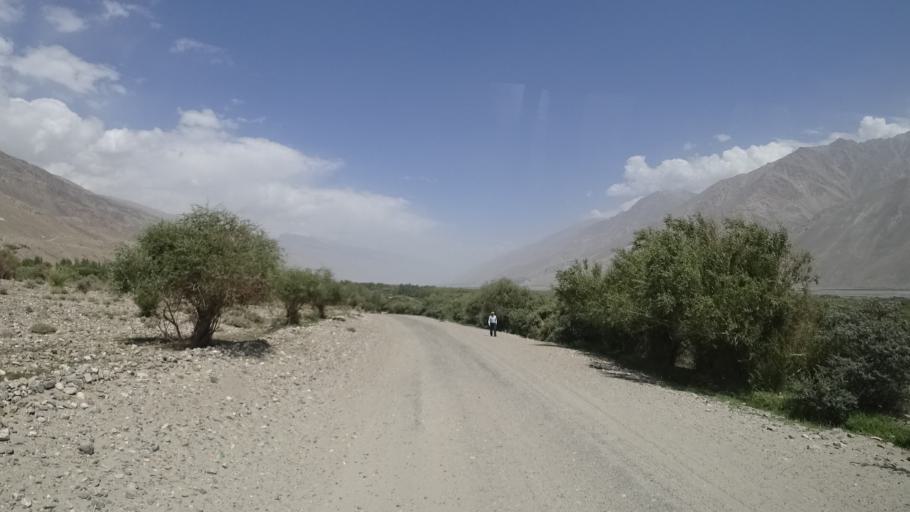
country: AF
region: Badakhshan
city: Khandud
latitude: 36.9113
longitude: 72.1779
